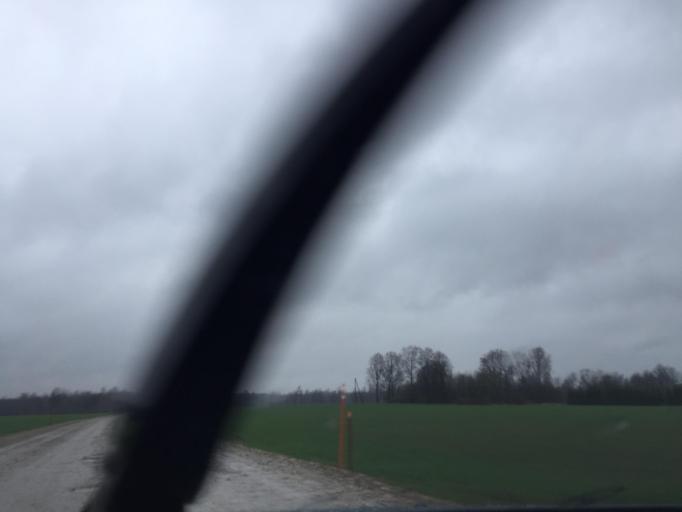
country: LV
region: Salacgrivas
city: Salacgriva
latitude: 57.7666
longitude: 24.5347
